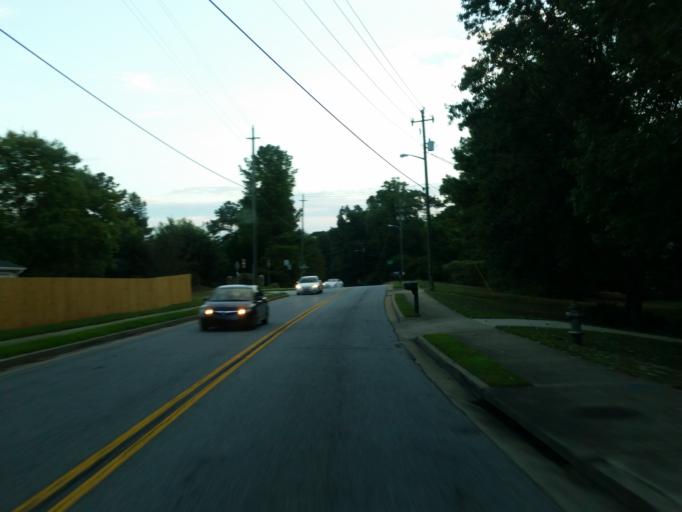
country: US
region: Georgia
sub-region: Cobb County
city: Marietta
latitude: 33.9630
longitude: -84.4631
